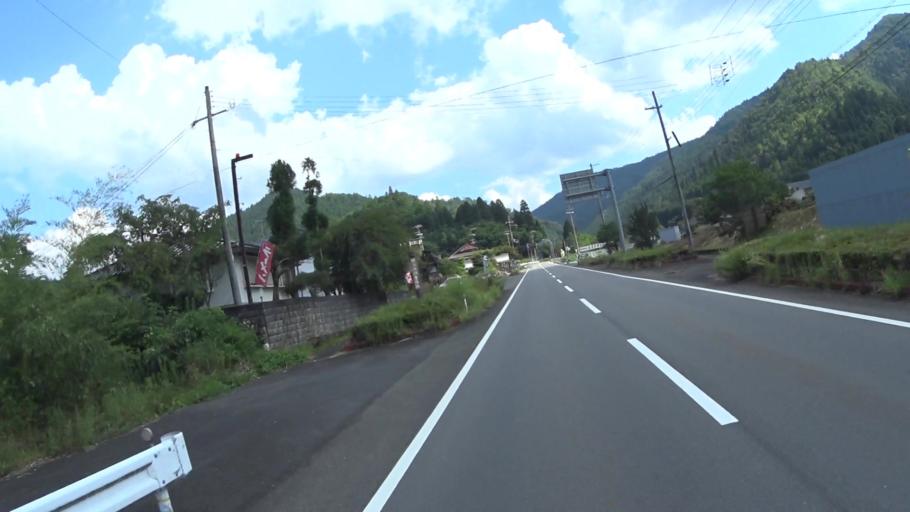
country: JP
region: Fukui
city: Obama
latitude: 35.2759
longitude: 135.5894
